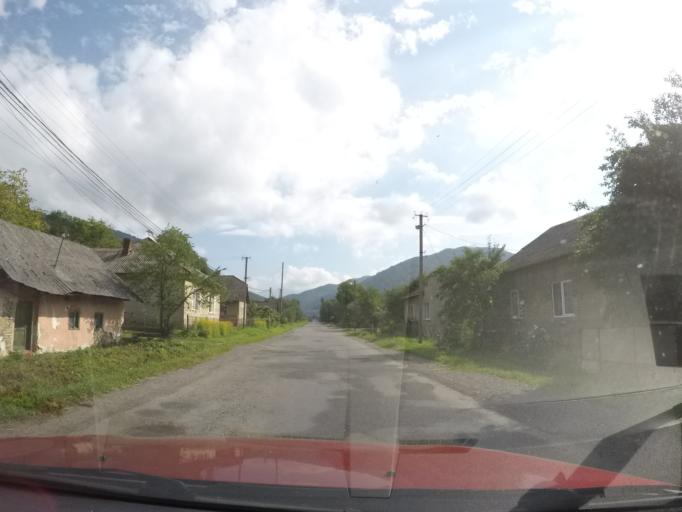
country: UA
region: Zakarpattia
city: Velykyi Bereznyi
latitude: 48.9453
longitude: 22.5991
